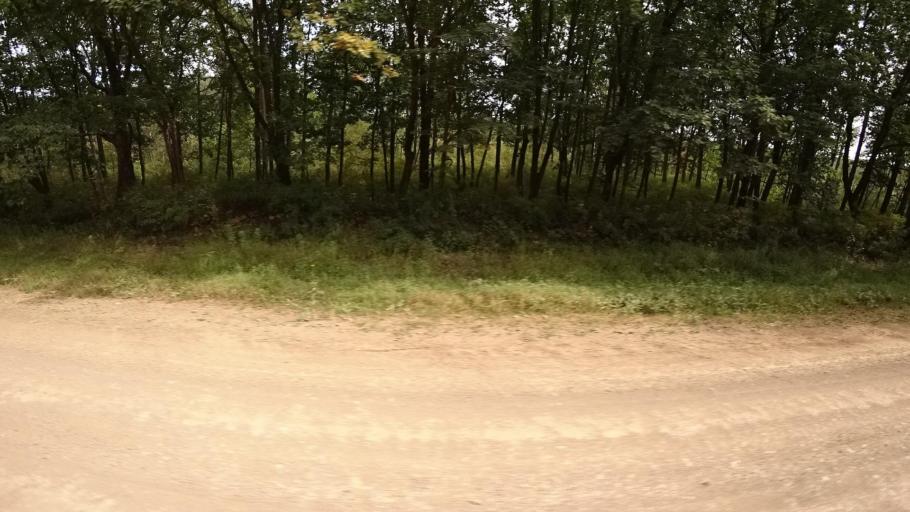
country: RU
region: Primorskiy
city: Yakovlevka
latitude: 44.4945
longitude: 133.5881
